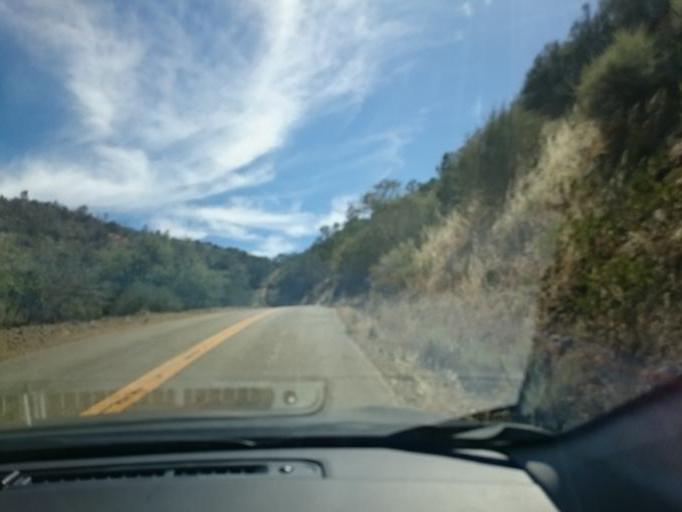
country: US
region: California
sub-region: Stanislaus County
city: Patterson
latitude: 37.4033
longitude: -121.4371
